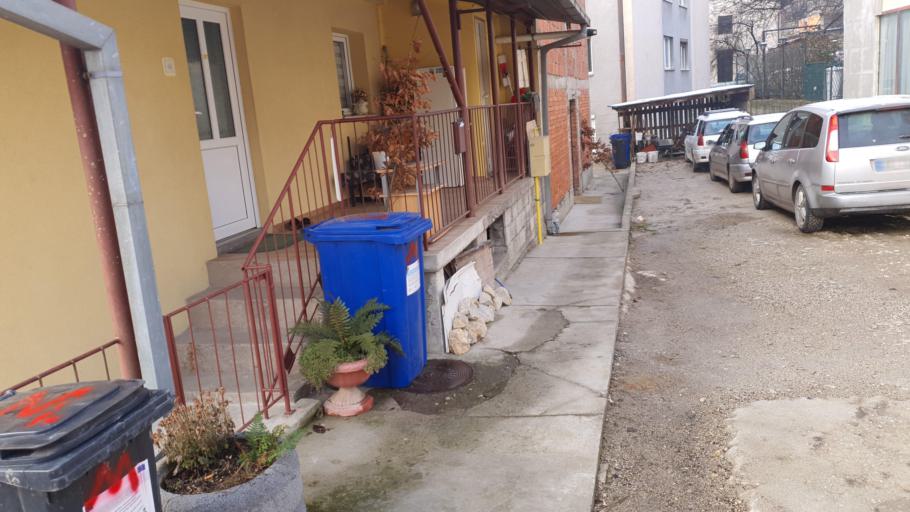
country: RS
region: Central Serbia
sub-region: Zlatiborski Okrug
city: Uzice
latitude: 43.8555
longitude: 19.8541
